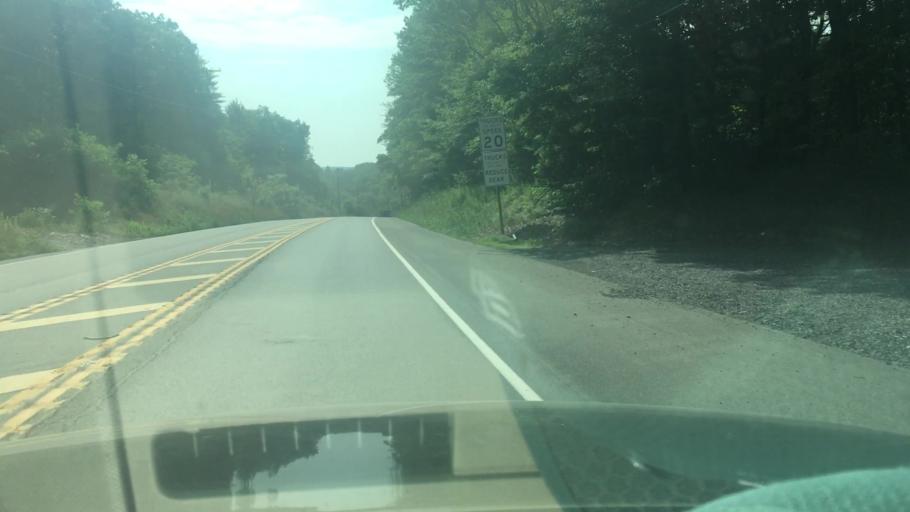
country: US
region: Pennsylvania
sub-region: Northumberland County
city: Kulpmont
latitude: 40.8151
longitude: -76.4565
